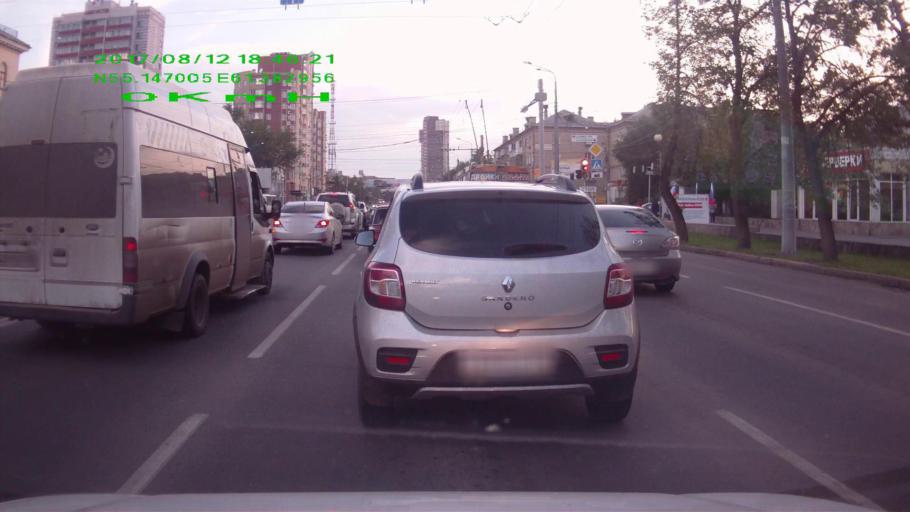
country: RU
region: Chelyabinsk
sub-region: Gorod Chelyabinsk
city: Chelyabinsk
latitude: 55.1455
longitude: 61.3810
